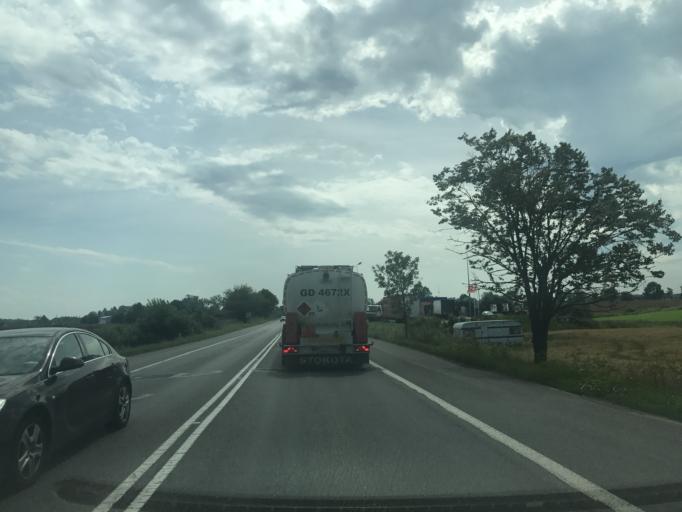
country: PL
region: Warmian-Masurian Voivodeship
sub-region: Powiat ostrodzki
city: Ostroda
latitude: 53.6527
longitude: 20.0516
